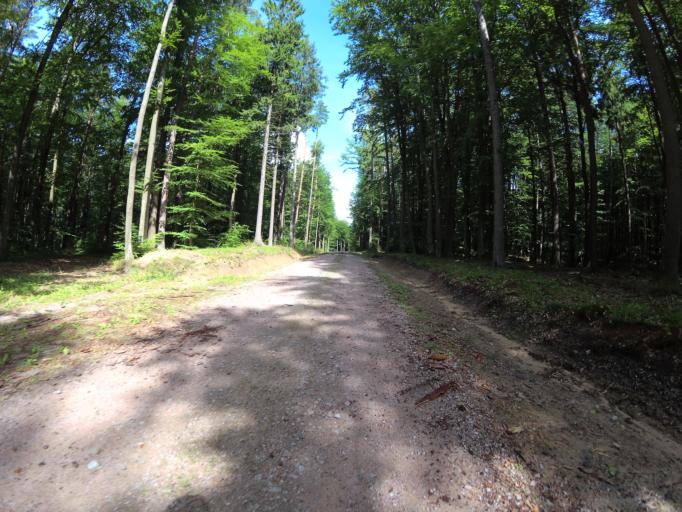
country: PL
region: Pomeranian Voivodeship
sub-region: Powiat wejherowski
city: Bojano
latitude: 54.5130
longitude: 18.4227
